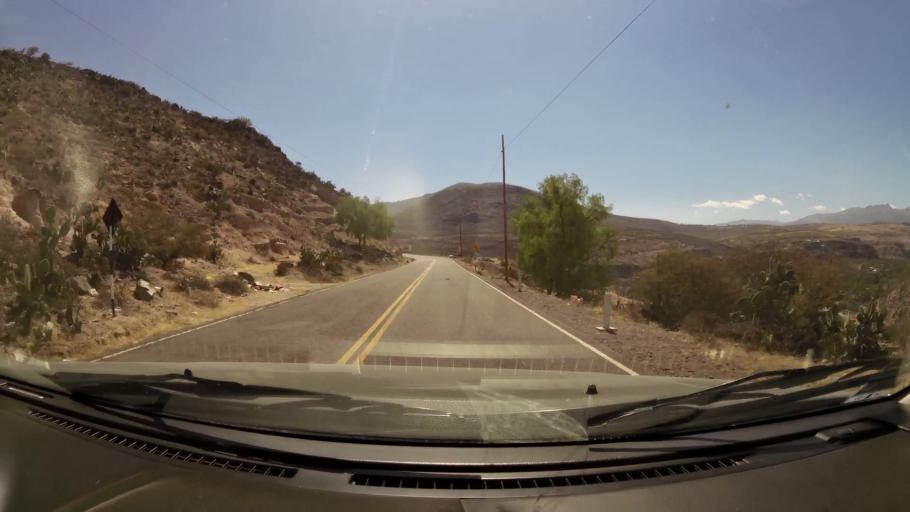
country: PE
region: Ayacucho
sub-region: Provincia de Huamanga
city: Pacaycasa
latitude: -13.0669
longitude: -74.2233
